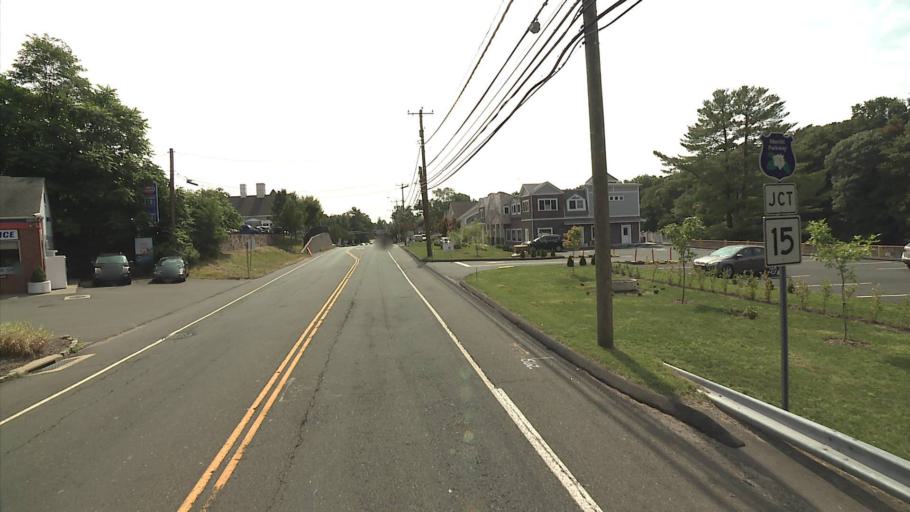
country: US
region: Connecticut
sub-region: Fairfield County
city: North Stamford
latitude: 41.1059
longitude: -73.5681
